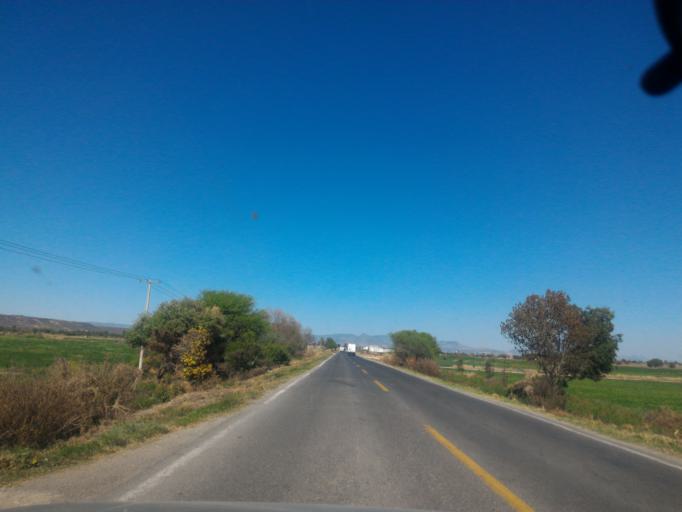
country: MX
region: Guanajuato
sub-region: San Francisco del Rincon
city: San Roque de Montes
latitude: 21.0185
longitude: -101.7929
